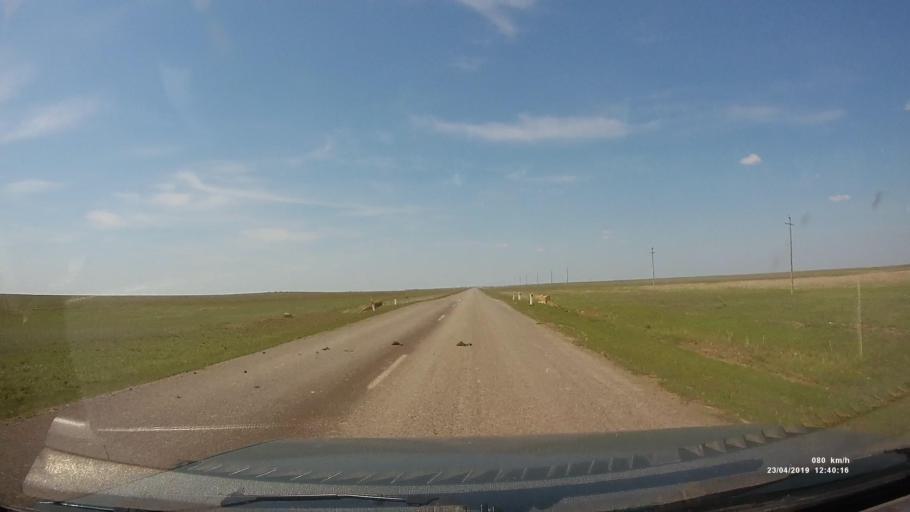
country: RU
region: Kalmykiya
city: Yashalta
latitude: 46.4393
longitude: 42.6985
